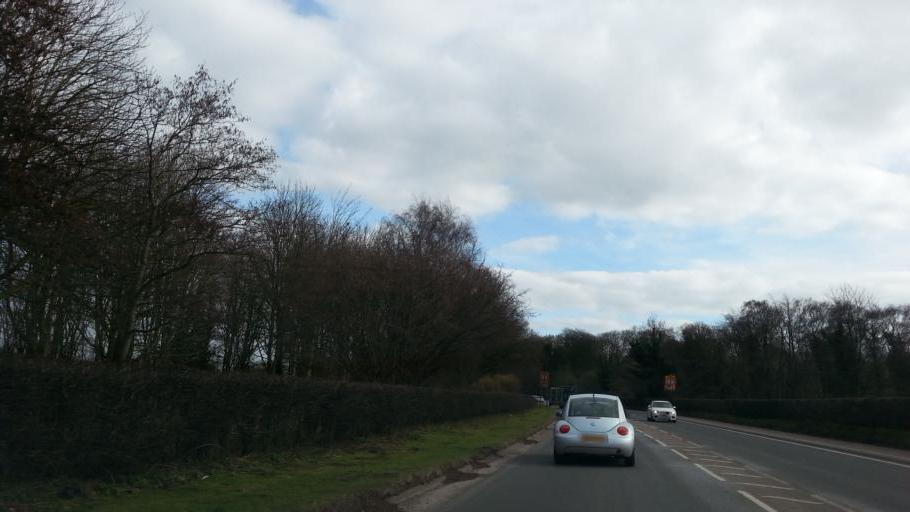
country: GB
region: England
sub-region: Staffordshire
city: Lichfield
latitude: 52.6838
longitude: -1.8427
